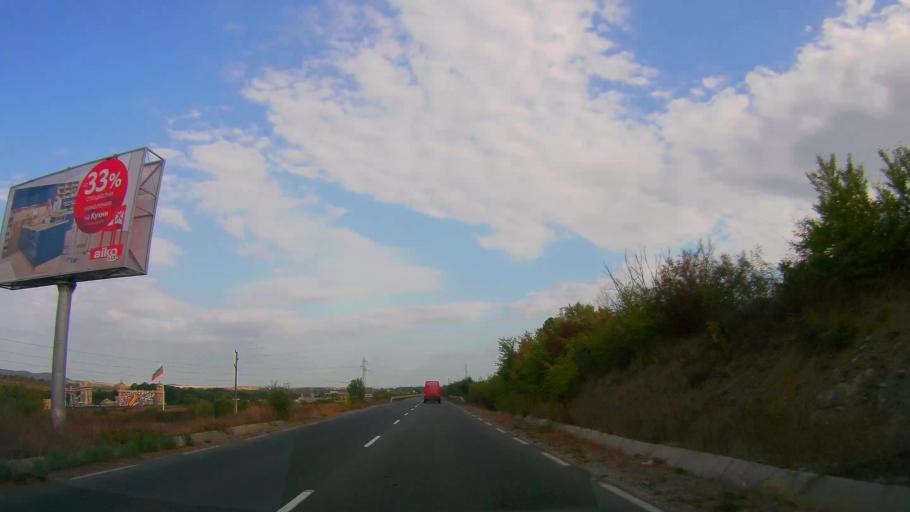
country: BG
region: Burgas
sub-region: Obshtina Sozopol
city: Sozopol
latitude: 42.3891
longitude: 27.6780
